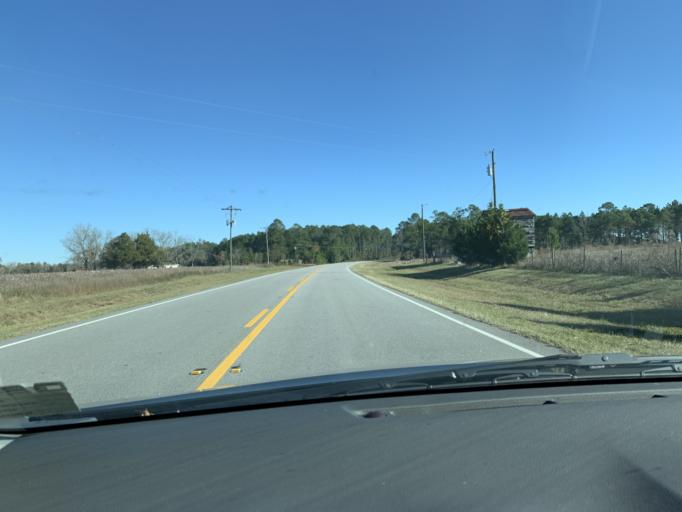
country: US
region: Georgia
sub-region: Ben Hill County
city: Fitzgerald
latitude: 31.7276
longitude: -83.1780
